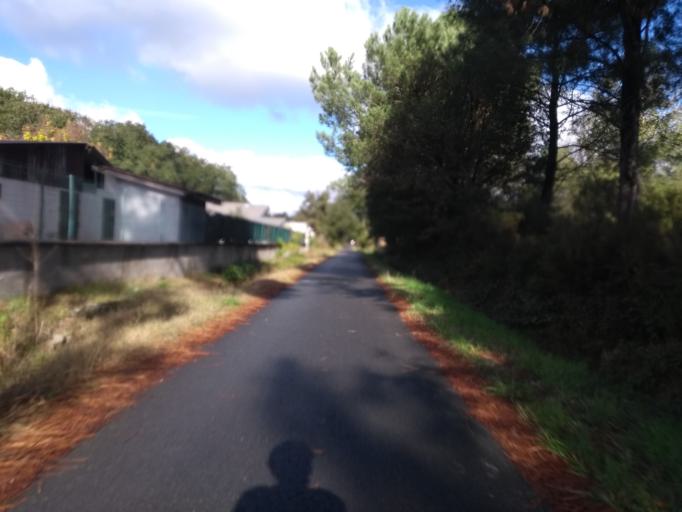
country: FR
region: Aquitaine
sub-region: Departement de la Gironde
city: Saint-Aubin-de-Medoc
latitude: 44.8019
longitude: -0.7080
